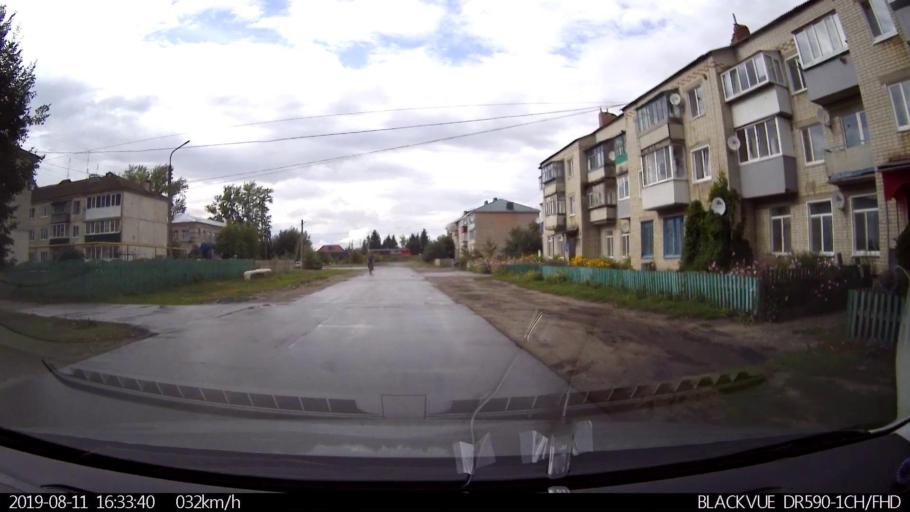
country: RU
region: Ulyanovsk
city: Mayna
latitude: 54.1155
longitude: 47.6246
